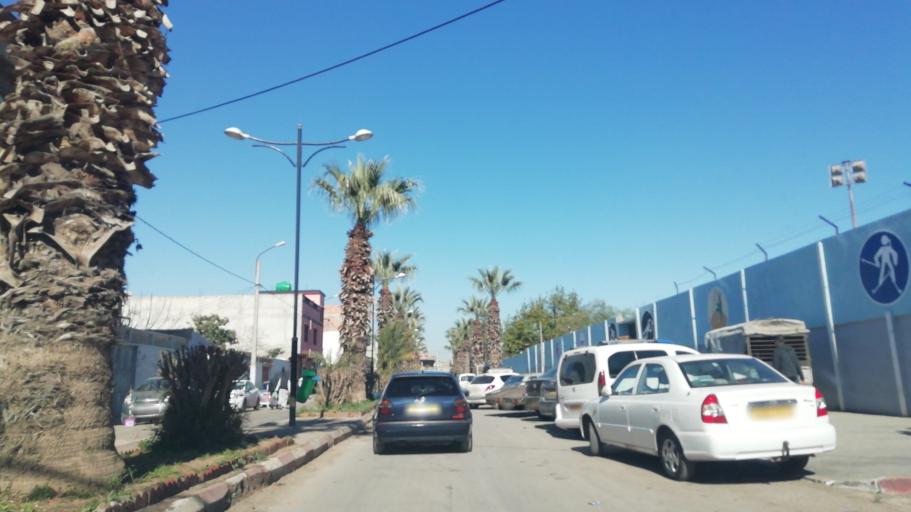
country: DZ
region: Oran
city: Es Senia
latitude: 35.6508
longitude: -0.6215
